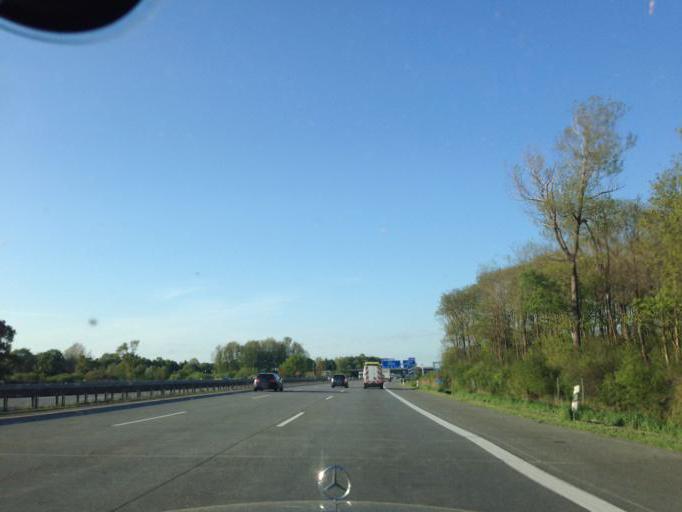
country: DE
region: Schleswig-Holstein
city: Hammoor
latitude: 53.7119
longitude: 10.3335
